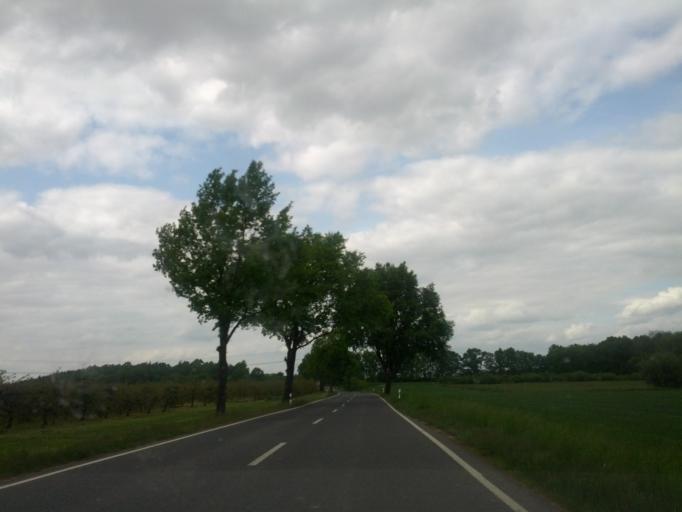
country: DE
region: Saxony
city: Kreischa
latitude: 50.9448
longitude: 13.7952
